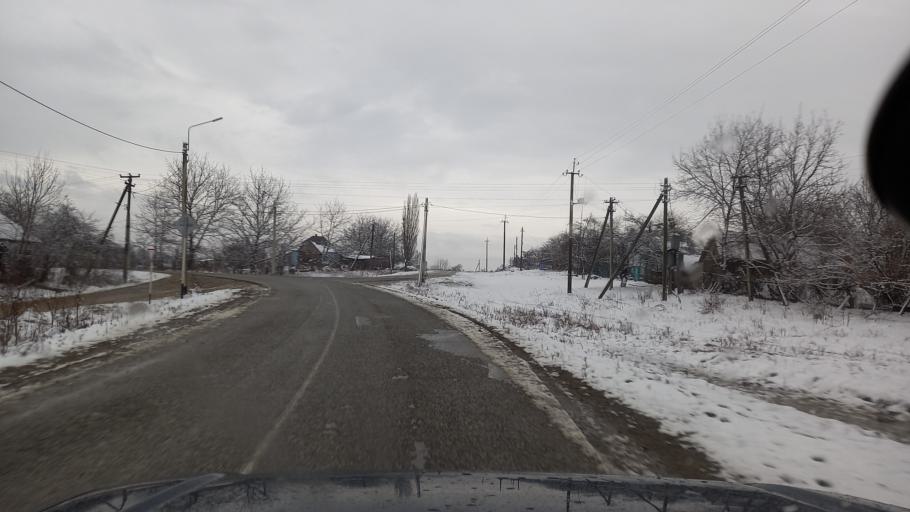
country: RU
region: Adygeya
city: Abadzekhskaya
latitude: 44.3467
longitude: 40.3201
